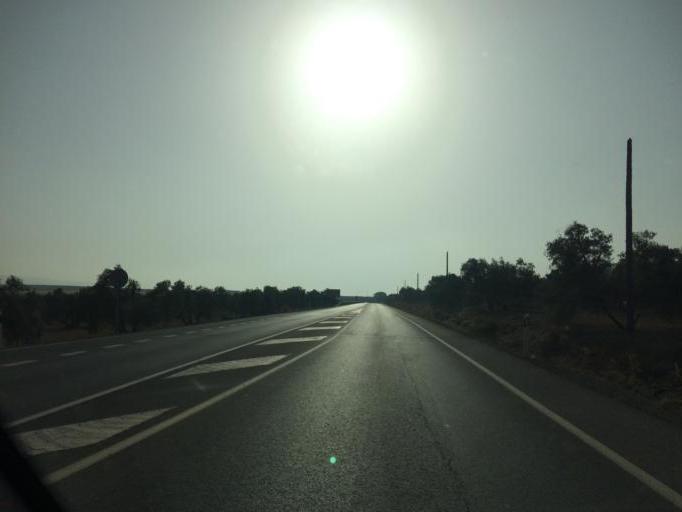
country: ES
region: Andalusia
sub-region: Provincia de Malaga
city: Humilladero
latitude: 37.0548
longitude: -4.7467
